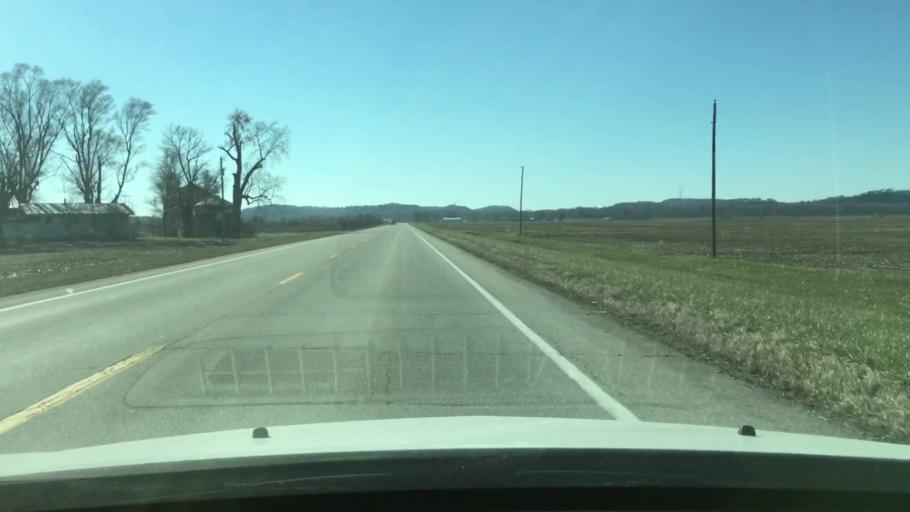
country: US
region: Missouri
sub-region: Pike County
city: Louisiana
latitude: 39.4777
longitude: -91.0195
